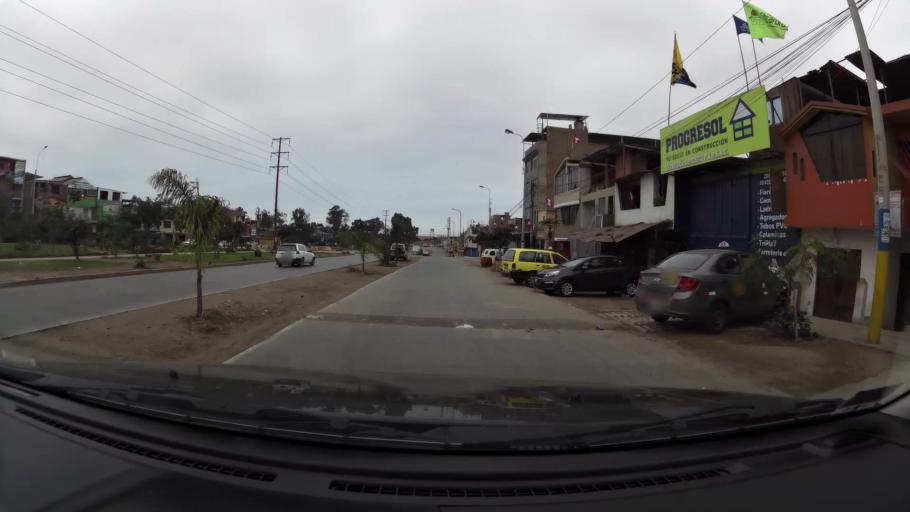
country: PE
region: Lima
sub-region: Lima
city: Surco
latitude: -12.1968
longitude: -76.9557
